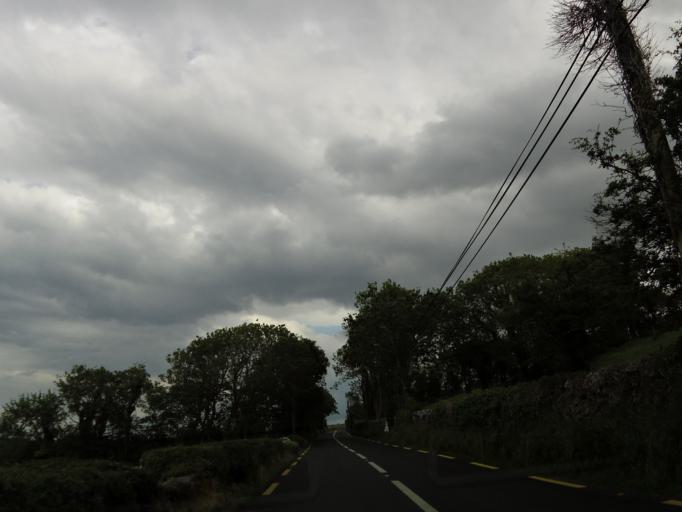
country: IE
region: Connaught
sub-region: County Galway
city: Bearna
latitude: 53.1352
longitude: -9.1089
